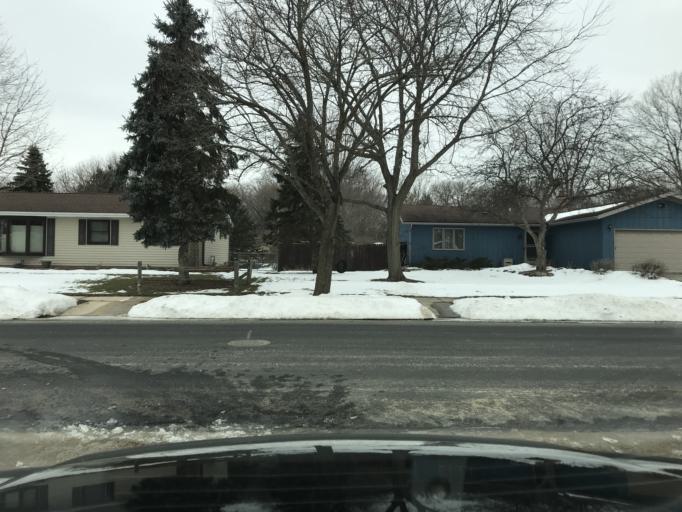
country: US
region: Wisconsin
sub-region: Dane County
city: Monona
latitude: 43.0745
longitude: -89.2850
